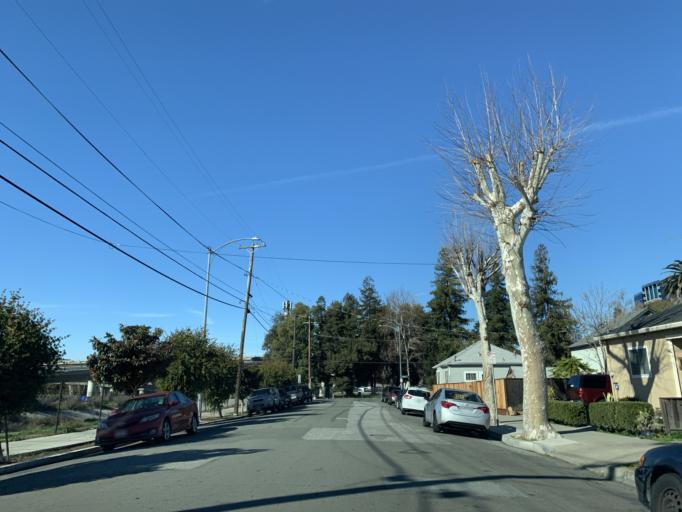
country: US
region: California
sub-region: Santa Clara County
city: San Jose
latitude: 37.3225
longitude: -121.8890
